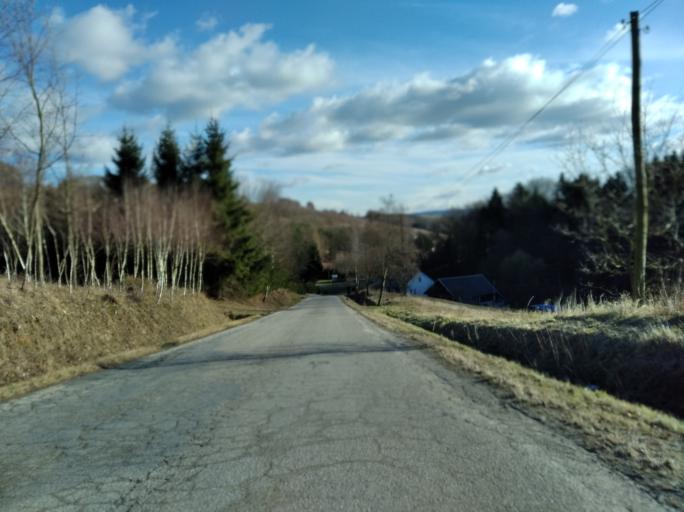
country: PL
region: Subcarpathian Voivodeship
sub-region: Powiat strzyzowski
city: Wisniowa
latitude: 49.8943
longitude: 21.7095
